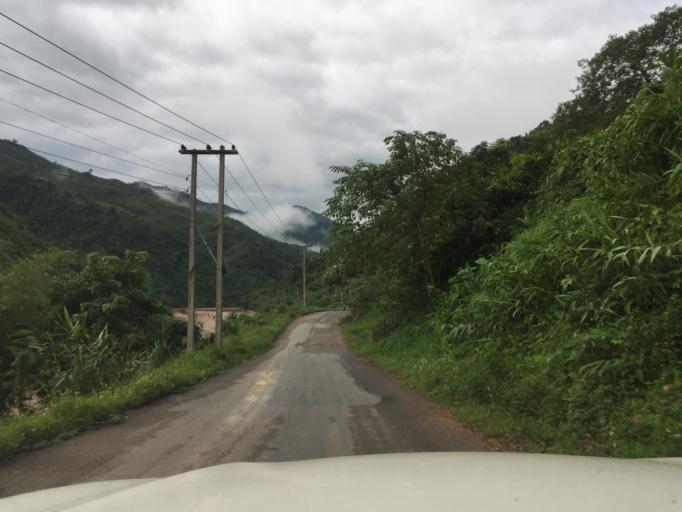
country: LA
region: Oudomxai
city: Muang La
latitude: 21.0648
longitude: 102.2397
